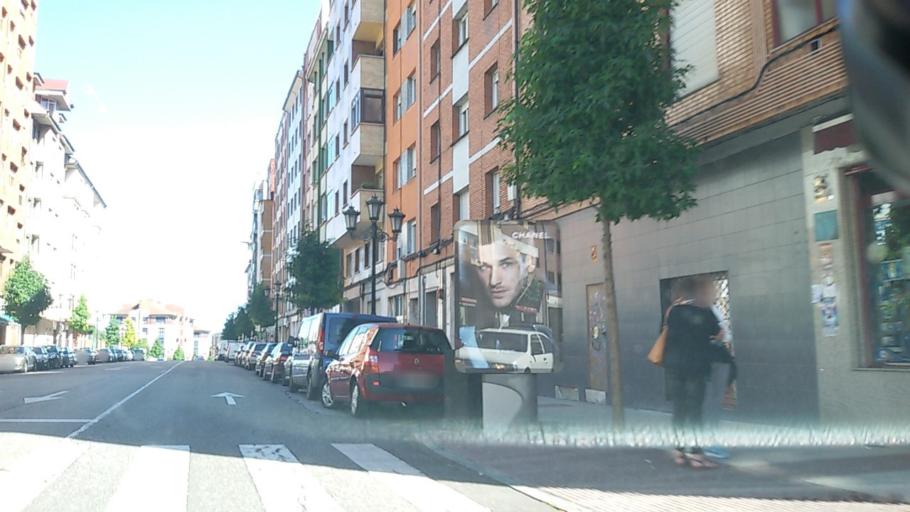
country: ES
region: Asturias
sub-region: Province of Asturias
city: Oviedo
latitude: 43.3738
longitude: -5.8365
